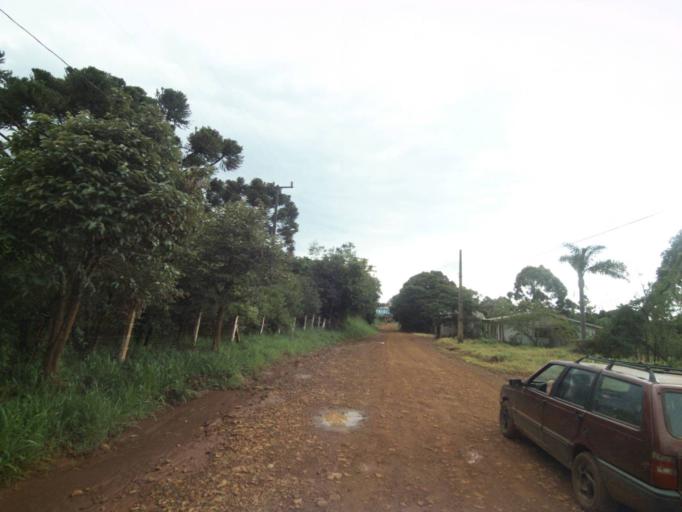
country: BR
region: Parana
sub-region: Pitanga
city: Pitanga
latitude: -24.8978
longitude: -51.9626
